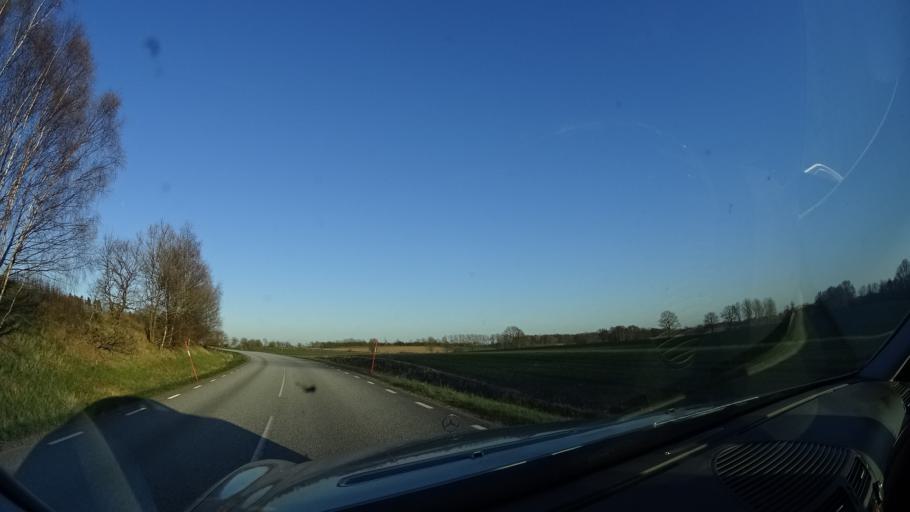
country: SE
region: Skane
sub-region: Klippans Kommun
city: Ljungbyhed
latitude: 55.9663
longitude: 13.2175
